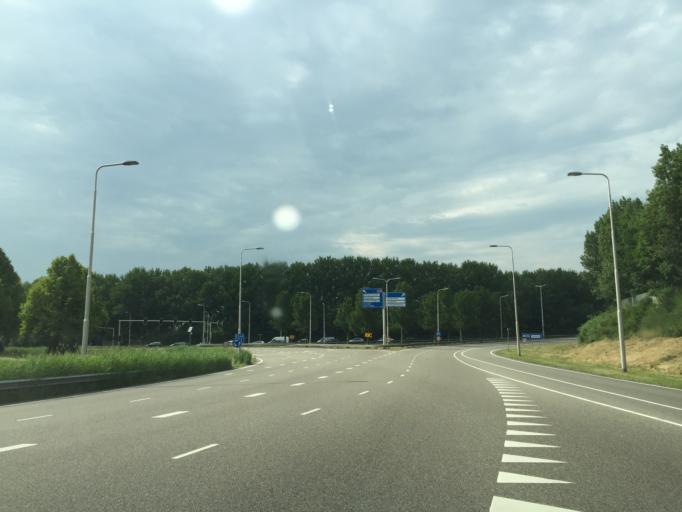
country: NL
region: Utrecht
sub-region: Gemeente Utrecht
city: Lunetten
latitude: 52.0569
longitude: 5.1243
